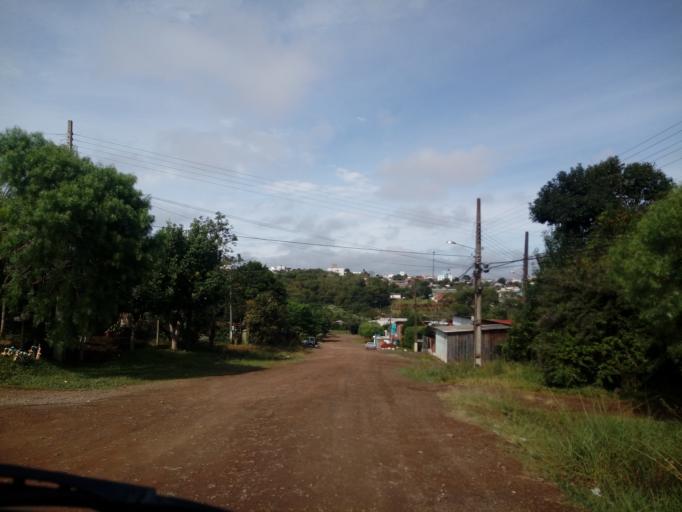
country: BR
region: Santa Catarina
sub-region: Chapeco
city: Chapeco
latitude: -27.0842
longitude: -52.6045
